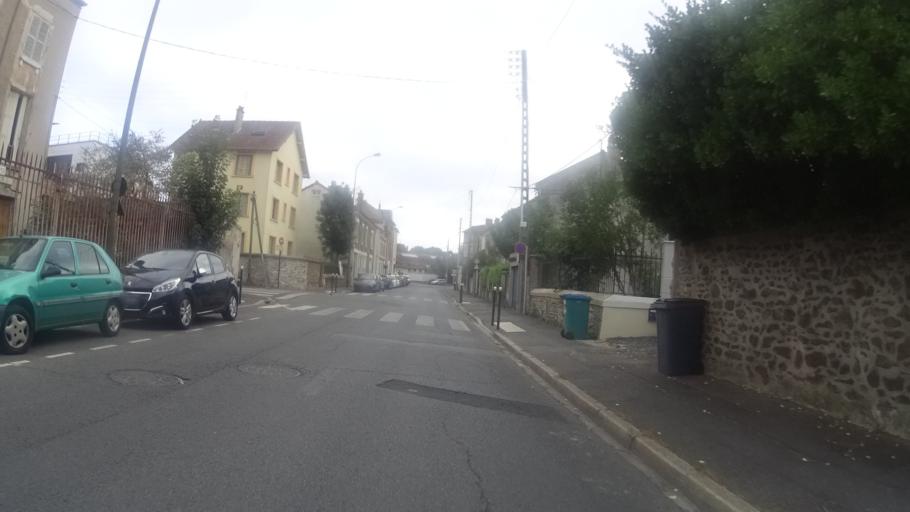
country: FR
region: Ile-de-France
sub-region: Departement de l'Essonne
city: Corbeil-Essonnes
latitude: 48.6098
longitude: 2.4716
